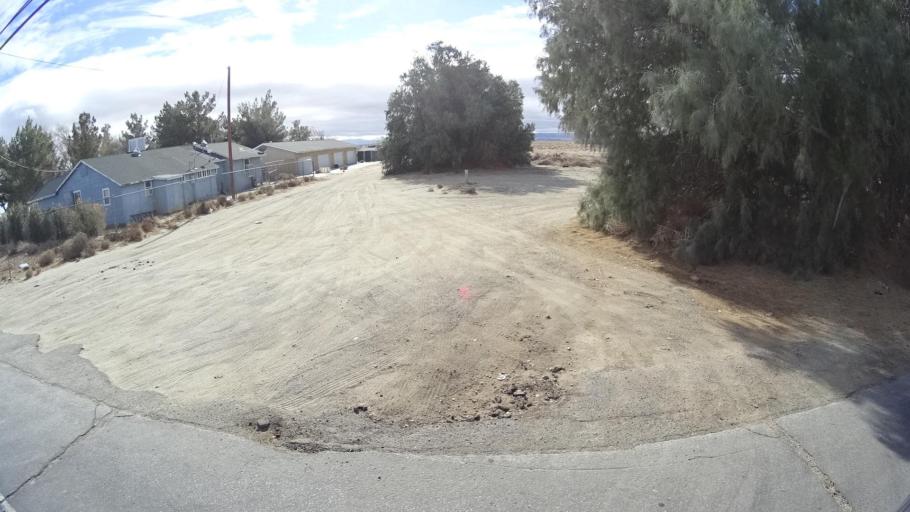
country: US
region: California
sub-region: Kern County
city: Rosamond
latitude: 34.8637
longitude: -118.2204
